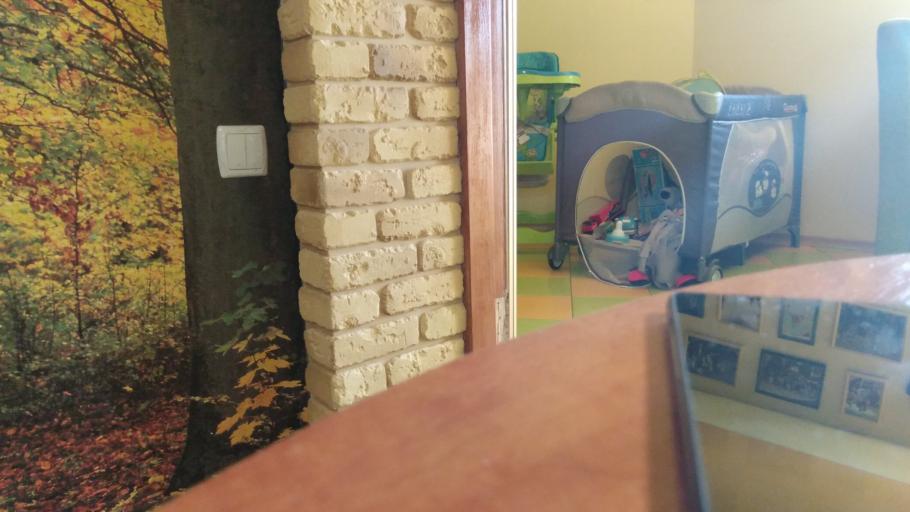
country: RU
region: Tverskaya
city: Bologoye
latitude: 57.9730
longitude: 34.1242
